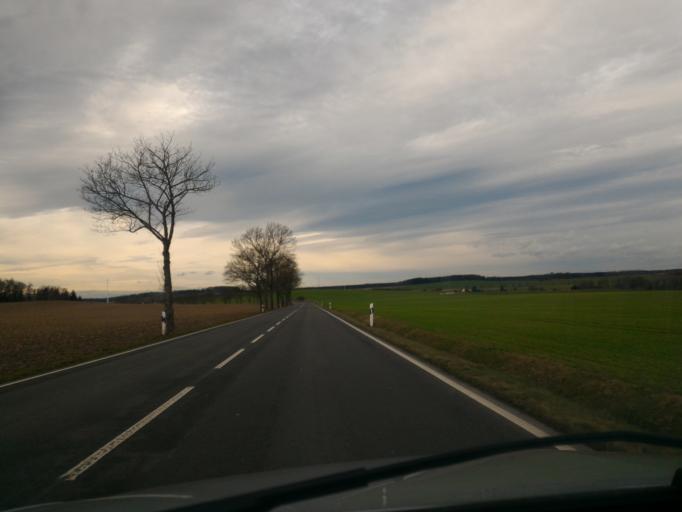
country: DE
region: Saxony
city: Frankenthal
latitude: 51.1121
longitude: 14.1249
